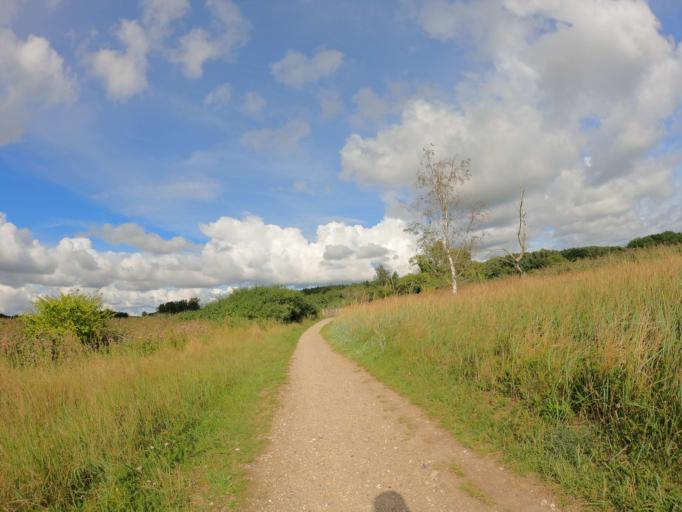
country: DE
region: Mecklenburg-Vorpommern
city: Putbus
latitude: 54.3429
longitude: 13.5357
